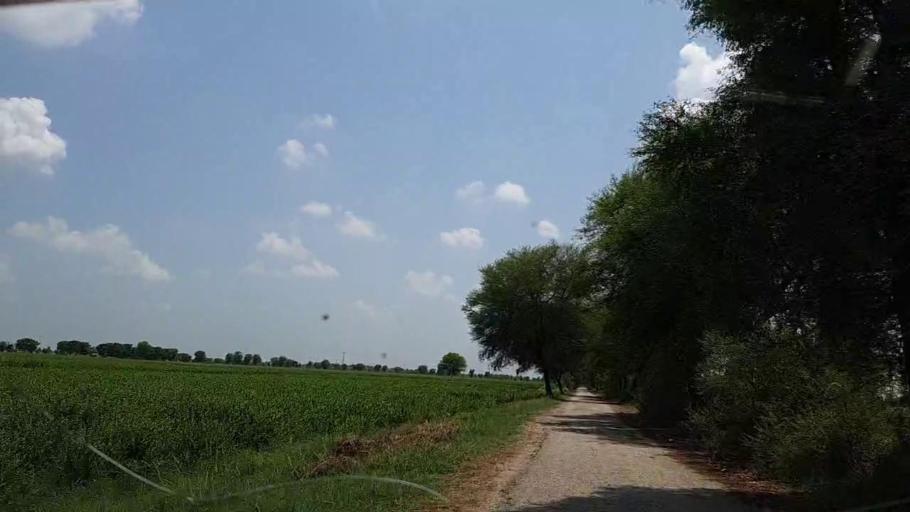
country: PK
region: Sindh
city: Tharu Shah
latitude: 27.0163
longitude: 68.0704
